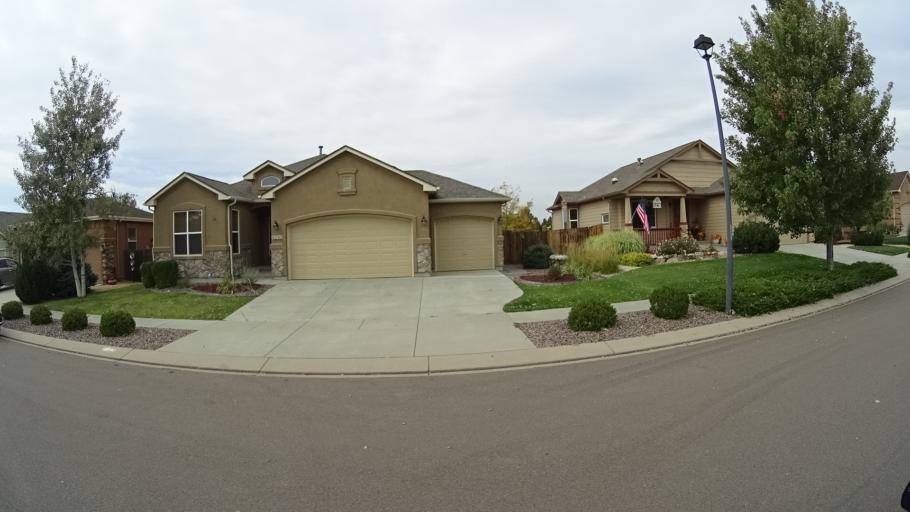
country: US
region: Colorado
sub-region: El Paso County
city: Cimarron Hills
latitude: 38.9192
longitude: -104.6914
